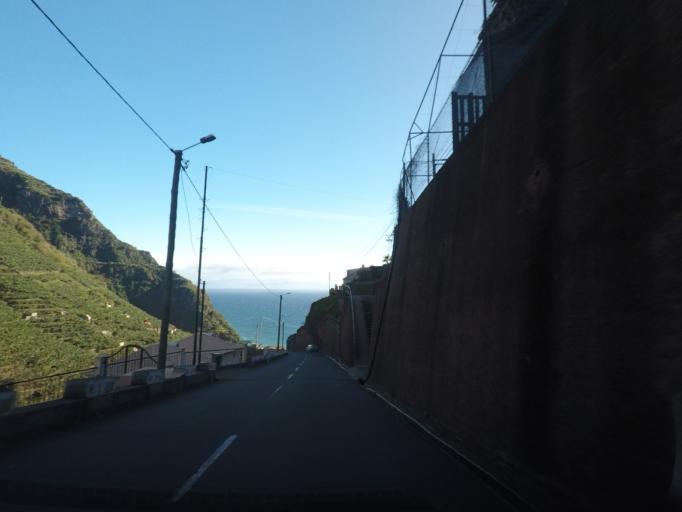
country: PT
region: Madeira
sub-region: Calheta
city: Arco da Calheta
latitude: 32.7080
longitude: -17.1350
